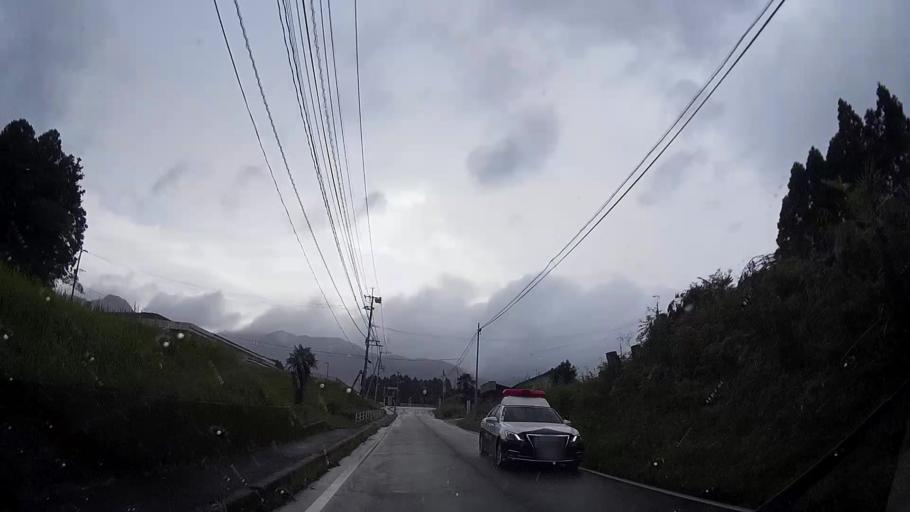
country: JP
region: Kumamoto
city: Aso
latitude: 32.8455
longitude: 131.0191
